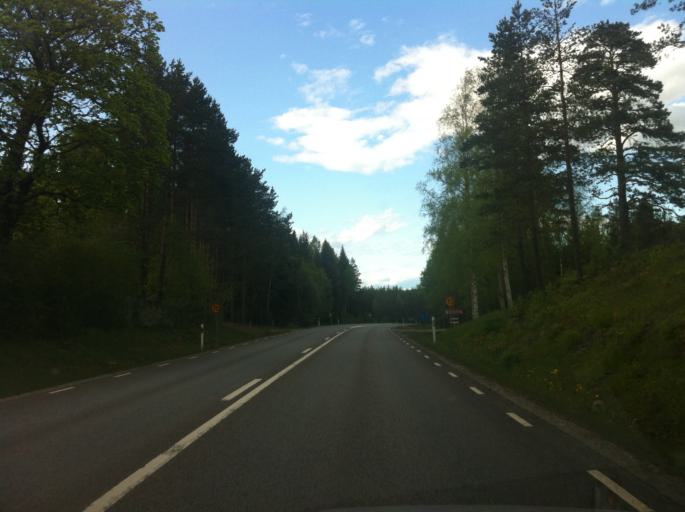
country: SE
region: Vaermland
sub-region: Filipstads Kommun
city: Filipstad
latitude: 59.7607
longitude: 14.2573
